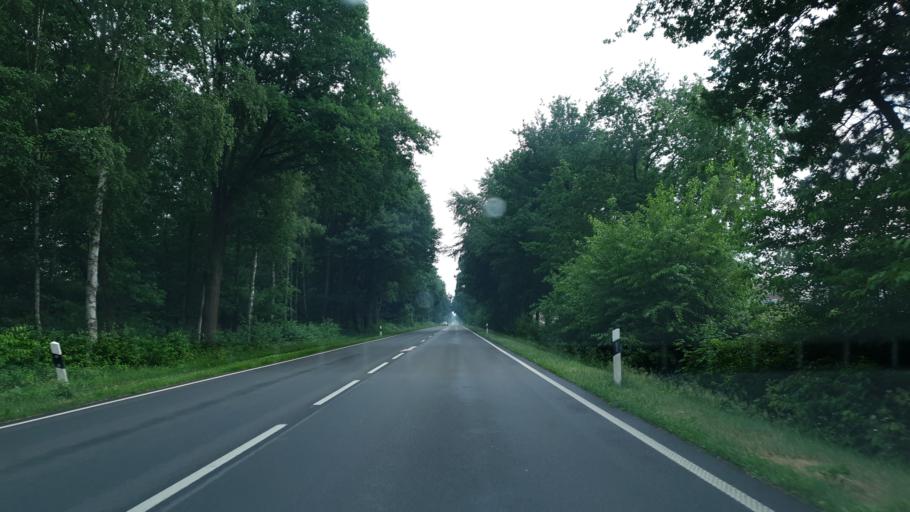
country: DE
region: Lower Saxony
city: Meppen
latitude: 52.6702
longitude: 7.3023
